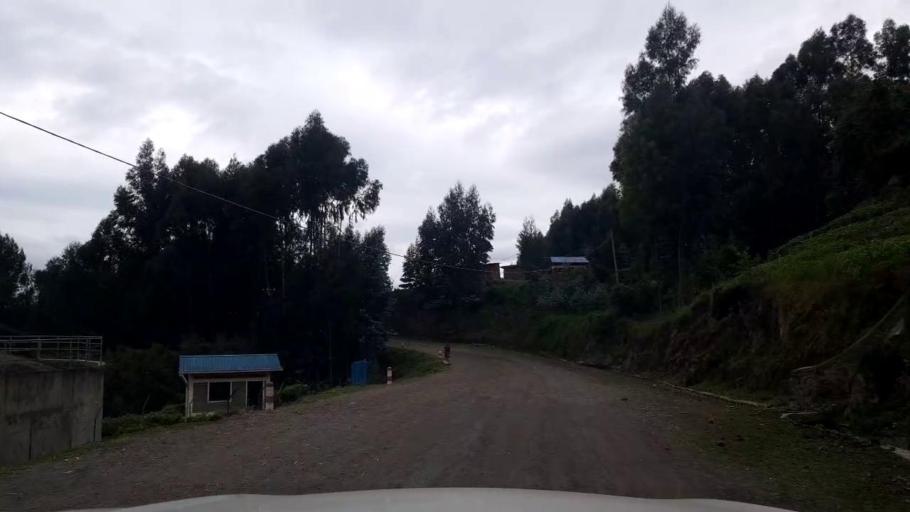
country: RW
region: Northern Province
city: Musanze
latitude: -1.5145
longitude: 29.5354
